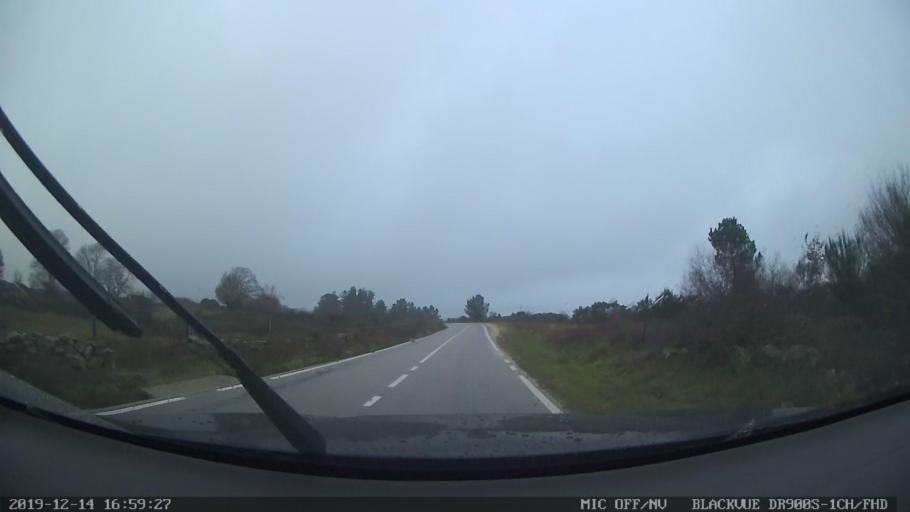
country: PT
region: Vila Real
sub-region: Vila Pouca de Aguiar
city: Vila Pouca de Aguiar
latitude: 41.4361
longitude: -7.5626
